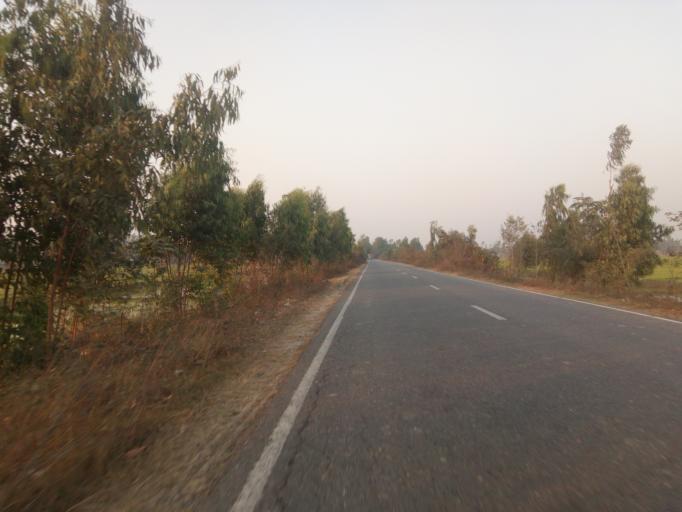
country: BD
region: Rajshahi
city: Bogra
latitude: 24.6137
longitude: 89.2407
